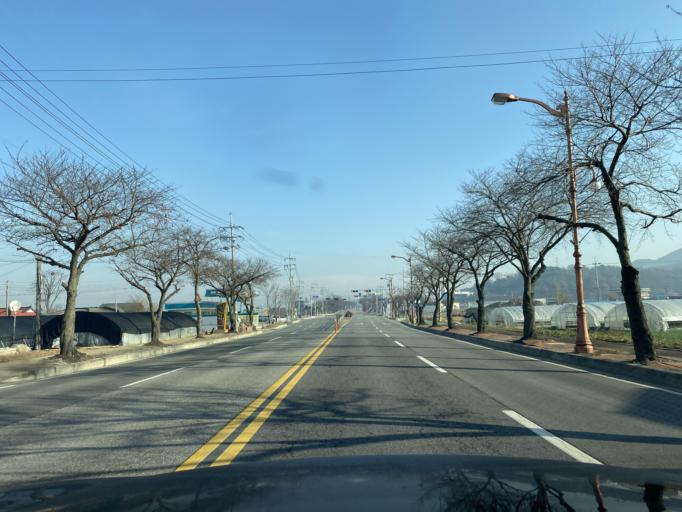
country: KR
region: Chungcheongnam-do
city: Yesan
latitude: 36.7193
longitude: 126.8459
